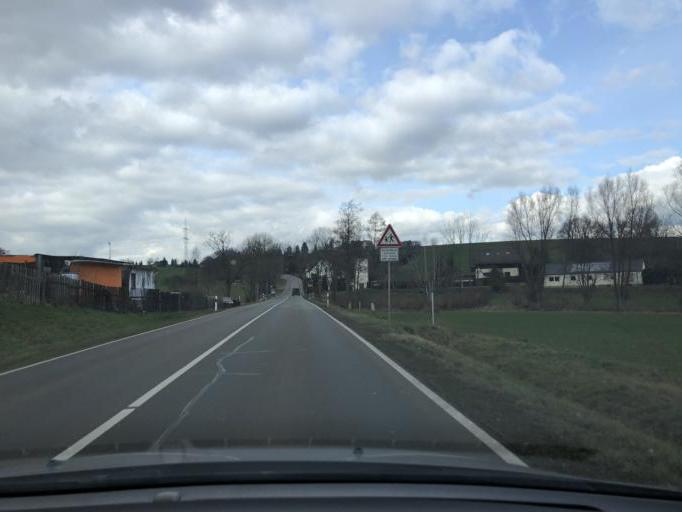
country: DE
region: Saxony
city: Dobeln
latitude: 51.1412
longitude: 13.0945
